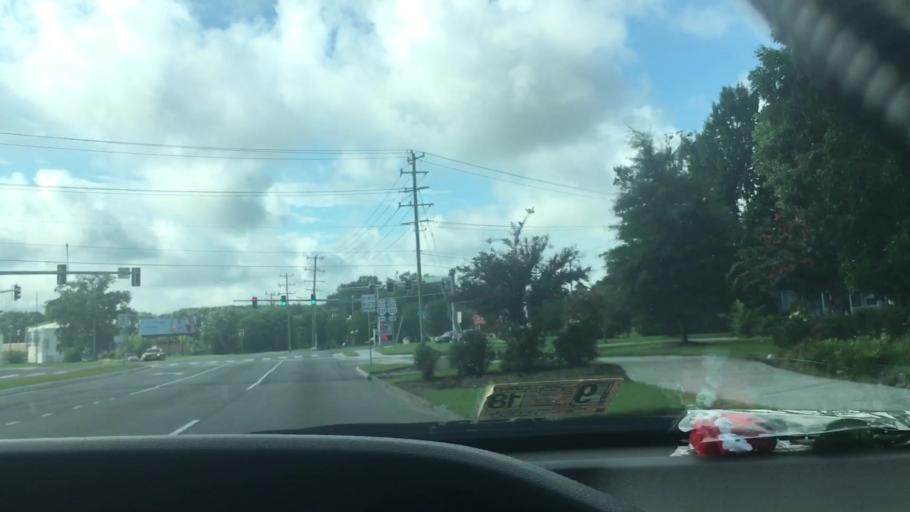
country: US
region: Virginia
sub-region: City of Portsmouth
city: Portsmouth Heights
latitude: 36.8258
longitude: -76.3390
